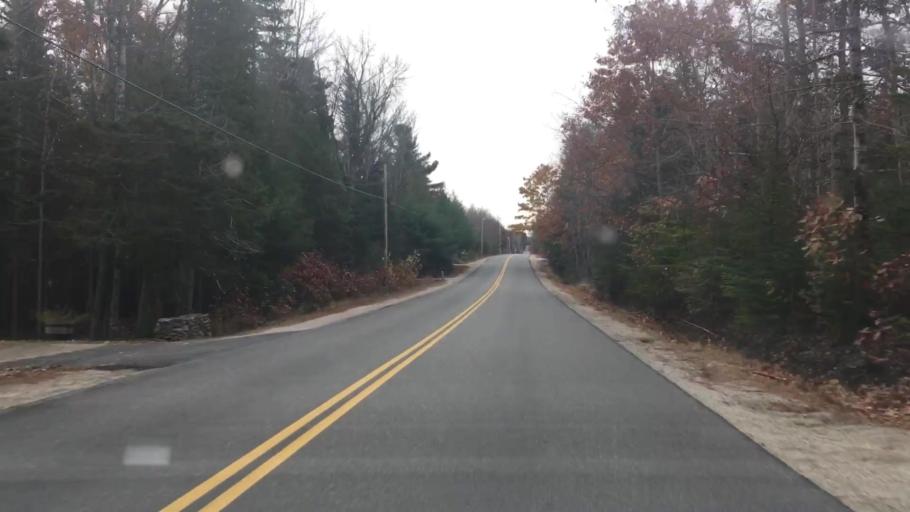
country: US
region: Maine
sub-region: Hancock County
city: Penobscot
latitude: 44.4573
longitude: -68.6378
